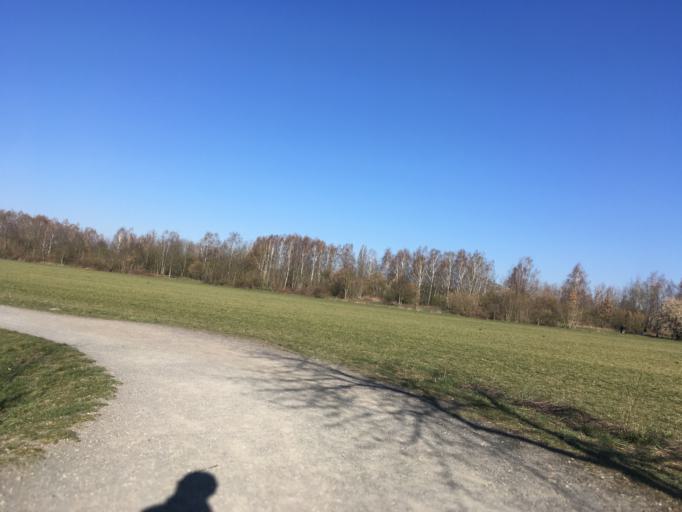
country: DE
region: Berlin
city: Blankenfelde
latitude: 52.6256
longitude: 13.4090
